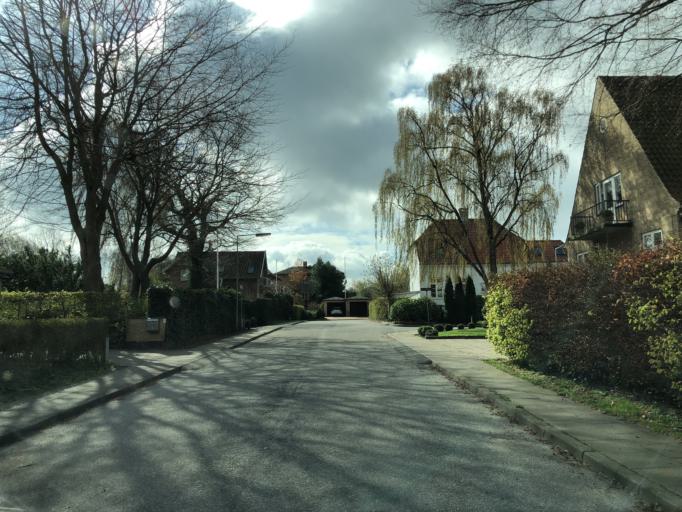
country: DK
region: North Denmark
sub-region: Alborg Kommune
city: Aalborg
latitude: 57.0489
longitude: 9.8967
